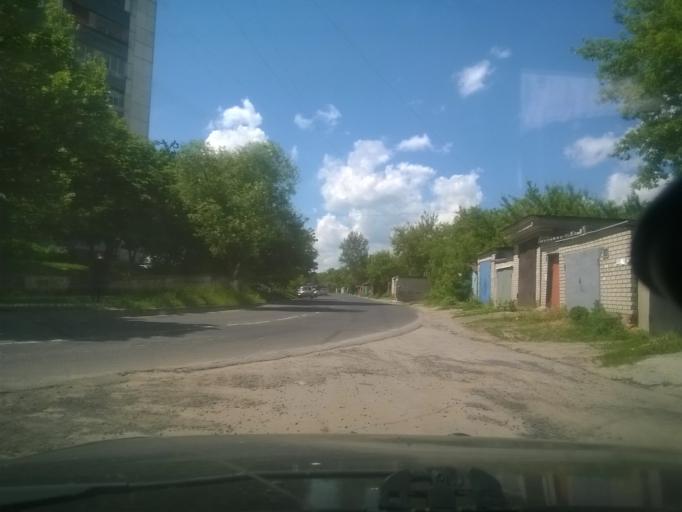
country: RU
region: Kursk
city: Kursk
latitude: 51.6795
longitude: 36.1464
